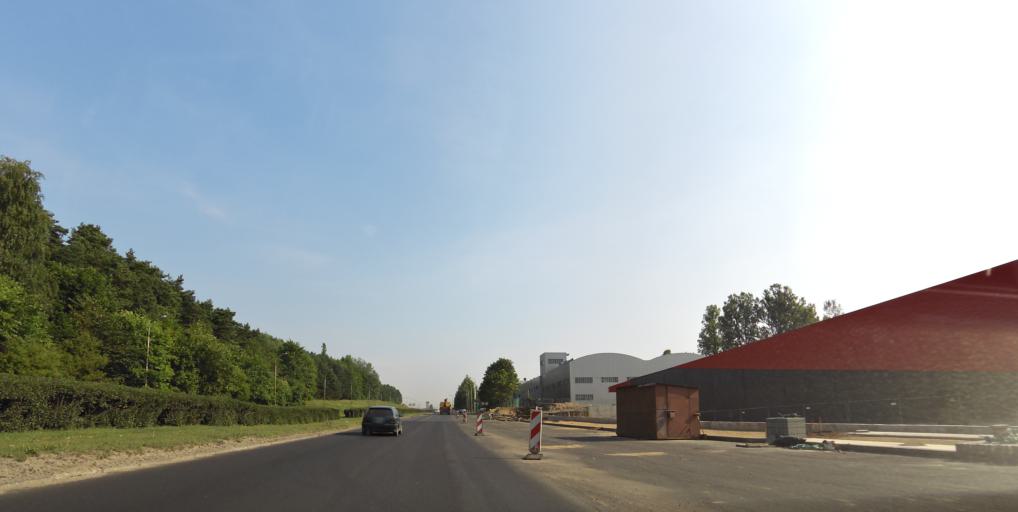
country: LT
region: Vilnius County
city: Seskine
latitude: 54.7058
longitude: 25.2668
